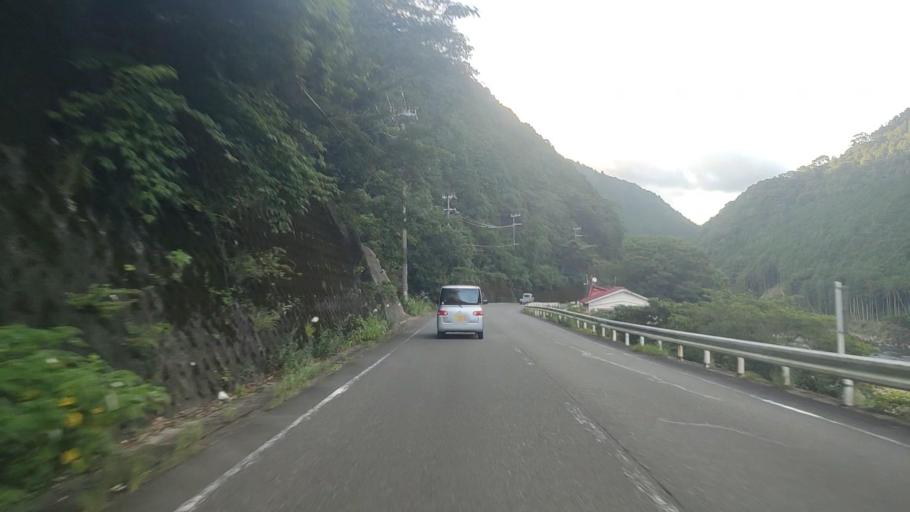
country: JP
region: Wakayama
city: Tanabe
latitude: 33.7667
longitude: 135.4998
